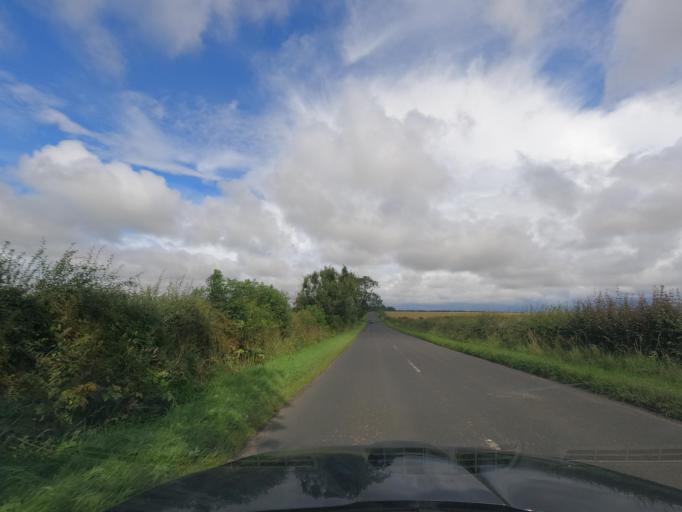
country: GB
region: England
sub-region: Northumberland
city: Lowick
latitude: 55.6280
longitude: -1.9888
